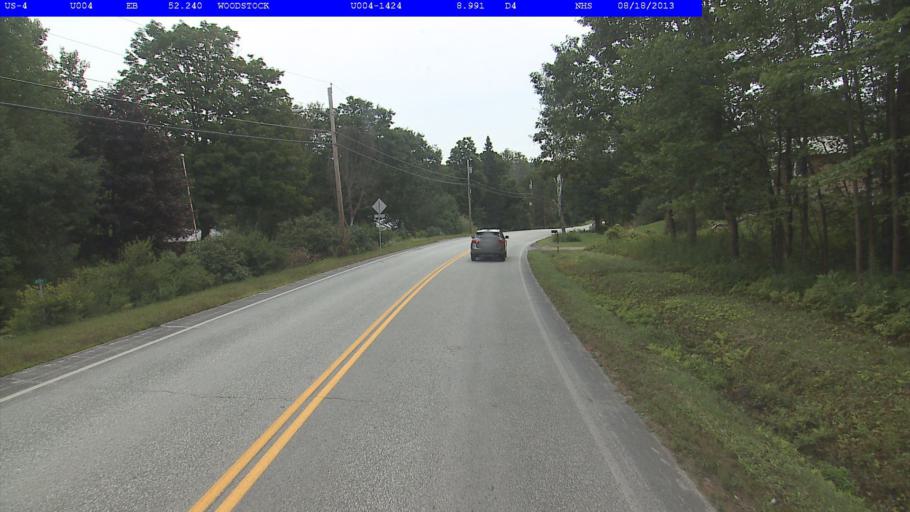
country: US
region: Vermont
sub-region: Windsor County
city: Woodstock
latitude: 43.6381
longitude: -72.4740
